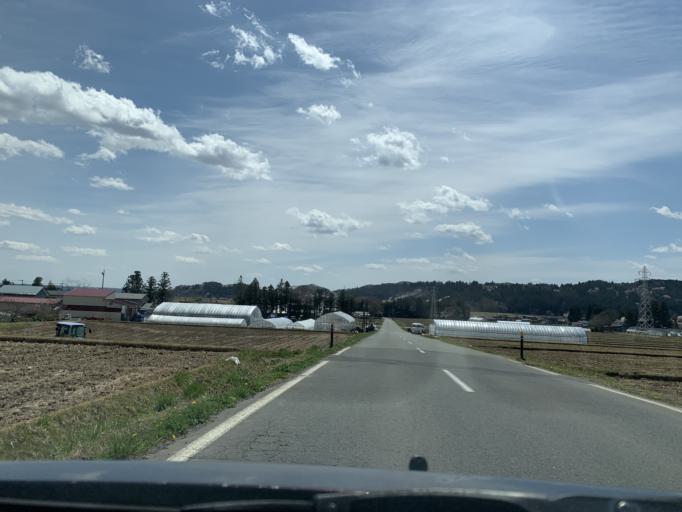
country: JP
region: Iwate
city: Ichinoseki
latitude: 39.0150
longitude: 141.1084
